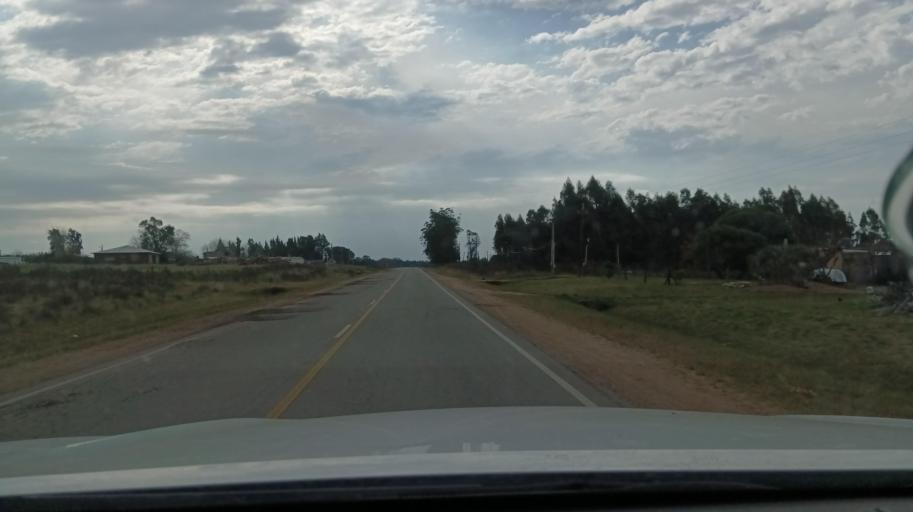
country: UY
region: Canelones
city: Toledo
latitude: -34.6844
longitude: -56.1110
